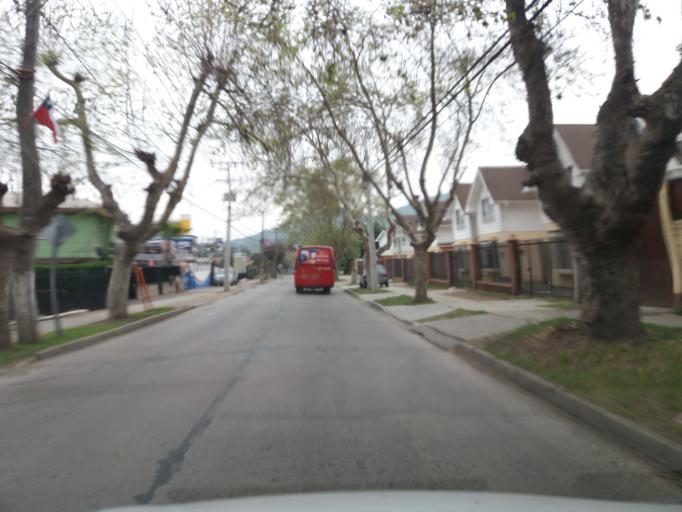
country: CL
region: Valparaiso
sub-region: Provincia de Quillota
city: Hacienda La Calera
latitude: -32.7984
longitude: -71.1464
